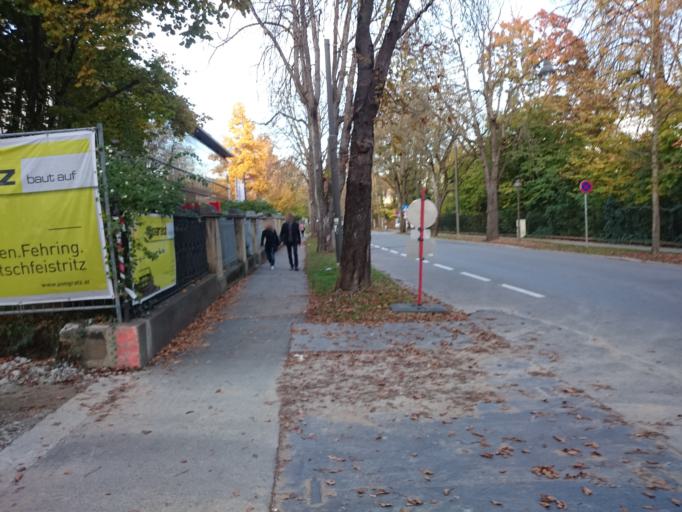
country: AT
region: Styria
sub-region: Graz Stadt
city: Graz
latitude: 47.0794
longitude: 15.4554
